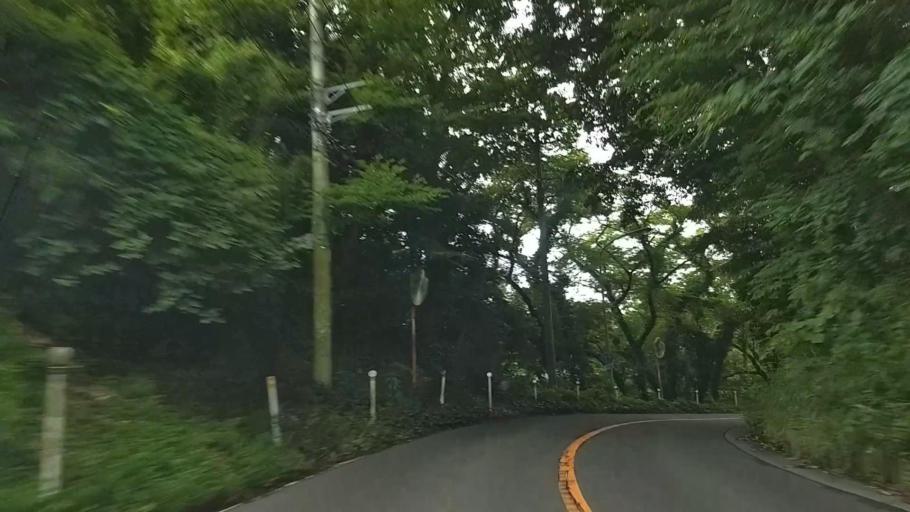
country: JP
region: Kanagawa
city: Ninomiya
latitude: 35.3345
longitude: 139.2383
